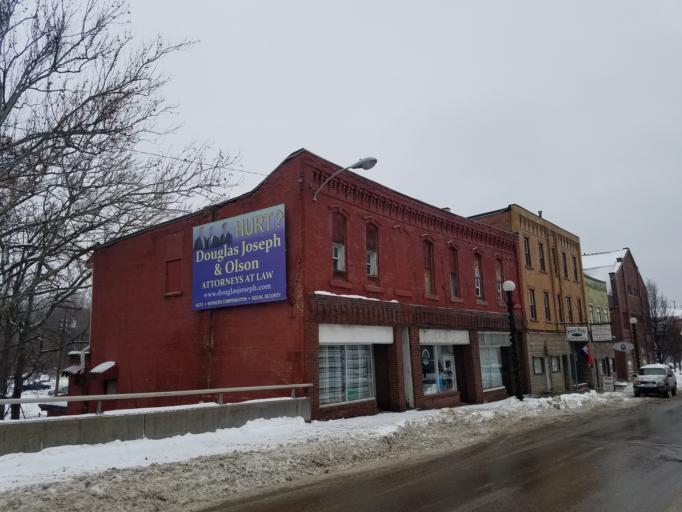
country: US
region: Pennsylvania
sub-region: Mercer County
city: Greenville
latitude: 41.4038
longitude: -80.3926
